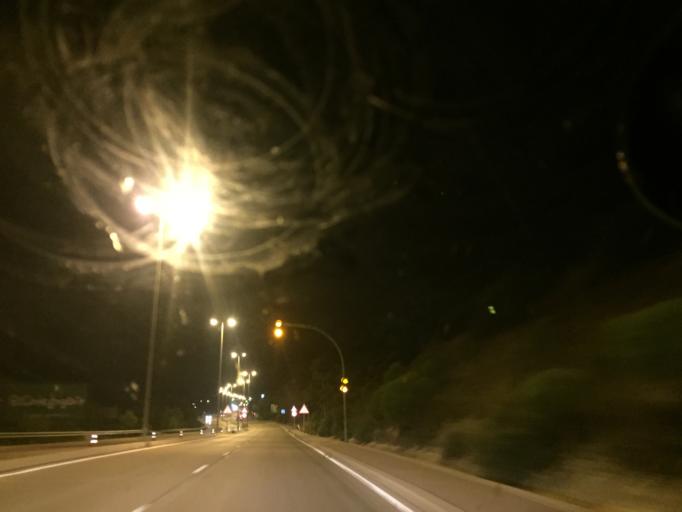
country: ES
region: Andalusia
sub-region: Provincia de Jaen
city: Jaen
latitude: 37.7818
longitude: -3.8213
